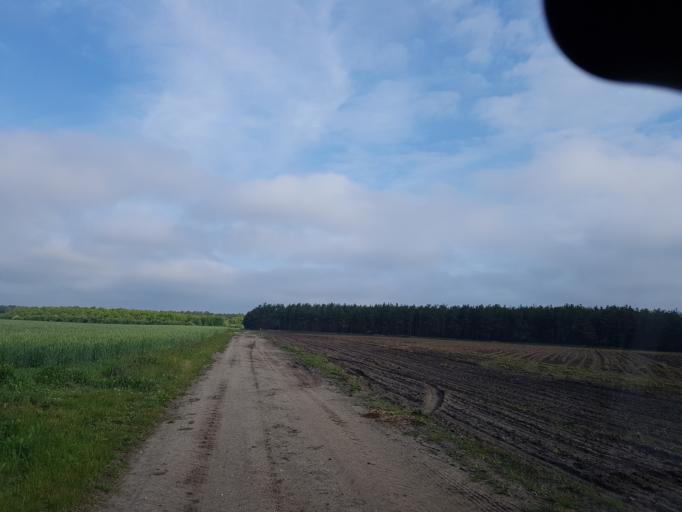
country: DE
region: Brandenburg
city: Finsterwalde
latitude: 51.5724
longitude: 13.6605
